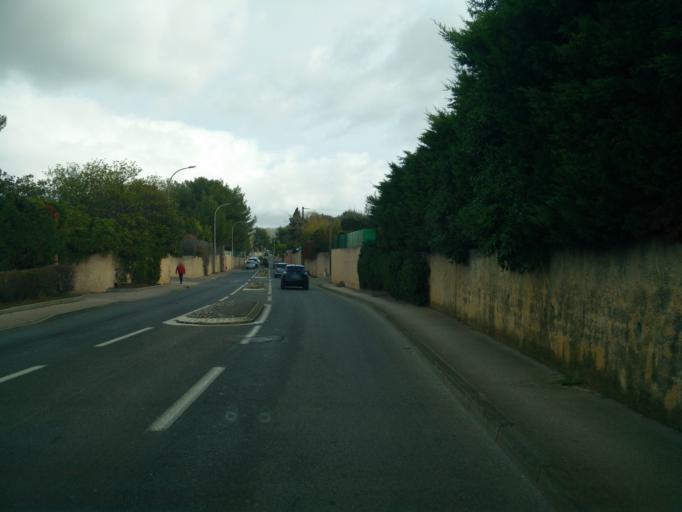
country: FR
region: Provence-Alpes-Cote d'Azur
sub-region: Departement du Var
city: Six-Fours-les-Plages
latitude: 43.0876
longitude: 5.8269
